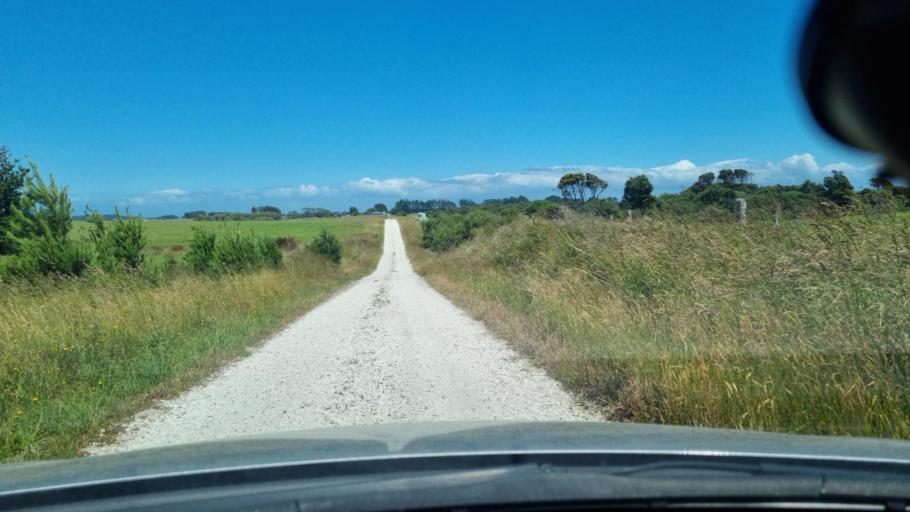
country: NZ
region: Southland
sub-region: Invercargill City
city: Invercargill
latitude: -46.4607
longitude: 168.4203
